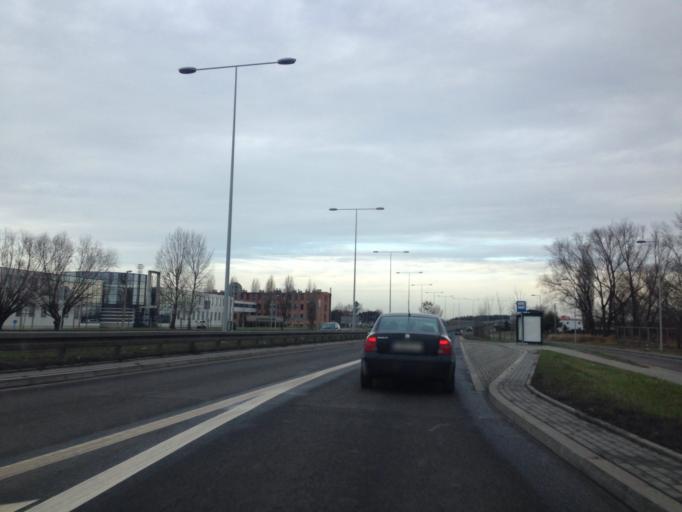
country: PL
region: Kujawsko-Pomorskie
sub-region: Torun
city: Torun
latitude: 52.9925
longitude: 18.6520
